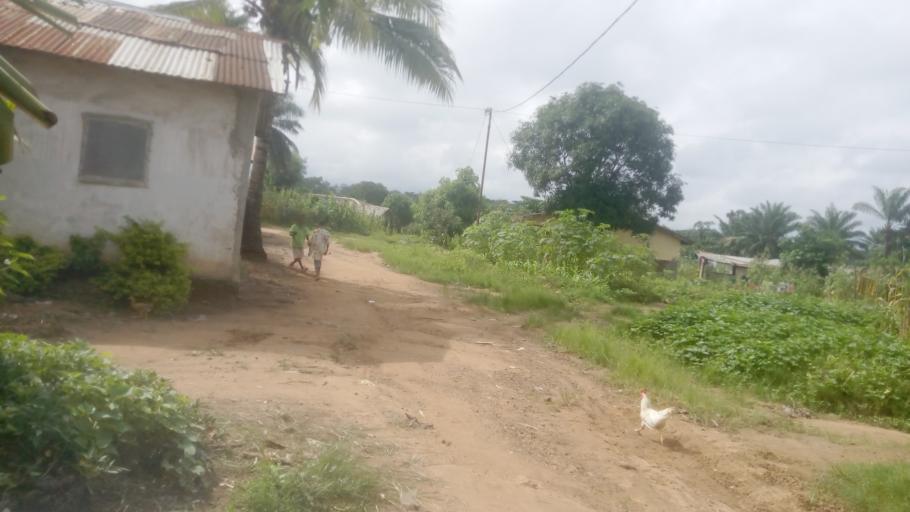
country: SL
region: Northern Province
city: Lunsar
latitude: 8.6951
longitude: -12.5375
